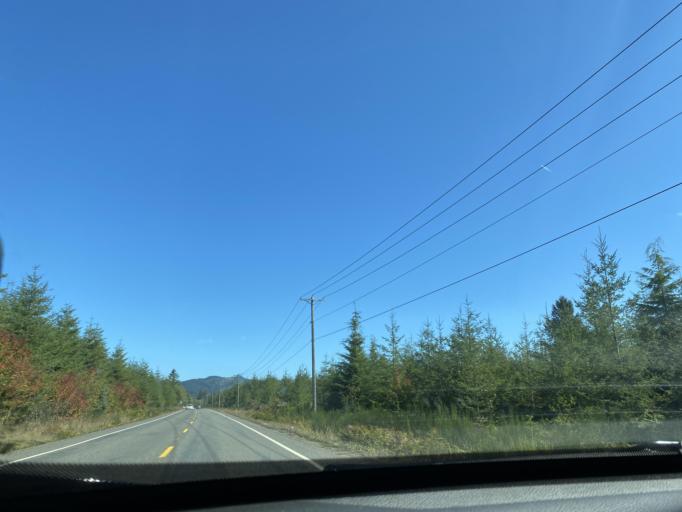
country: US
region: Washington
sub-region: Clallam County
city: Forks
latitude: 47.9641
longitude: -124.4182
